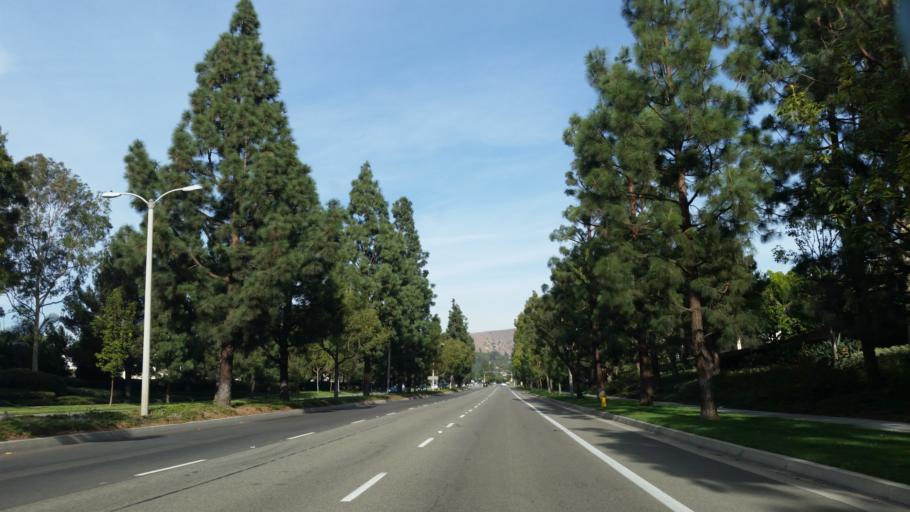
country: US
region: California
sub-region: Orange County
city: North Tustin
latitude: 33.7263
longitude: -117.7660
